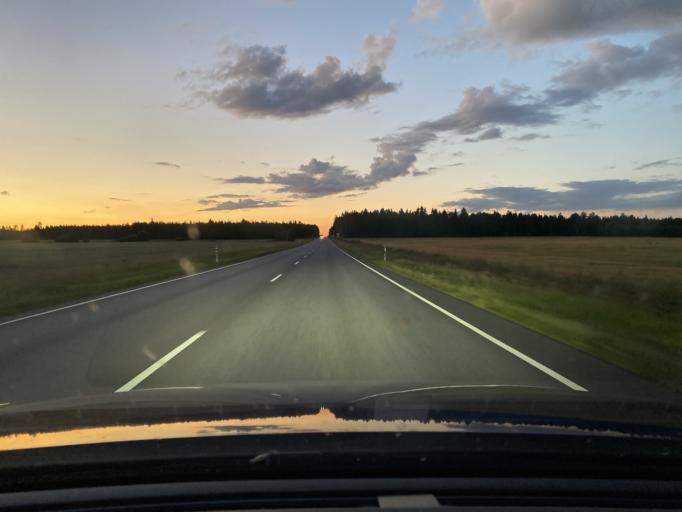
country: FI
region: Satakunta
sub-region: Pori
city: Vampula
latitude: 60.9417
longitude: 22.6833
